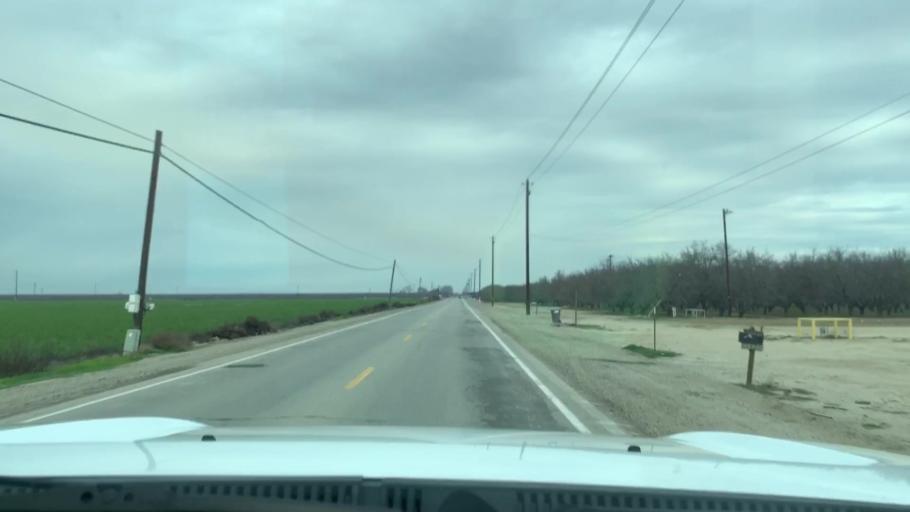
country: US
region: California
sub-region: Kern County
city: Rosedale
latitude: 35.3921
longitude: -119.2520
